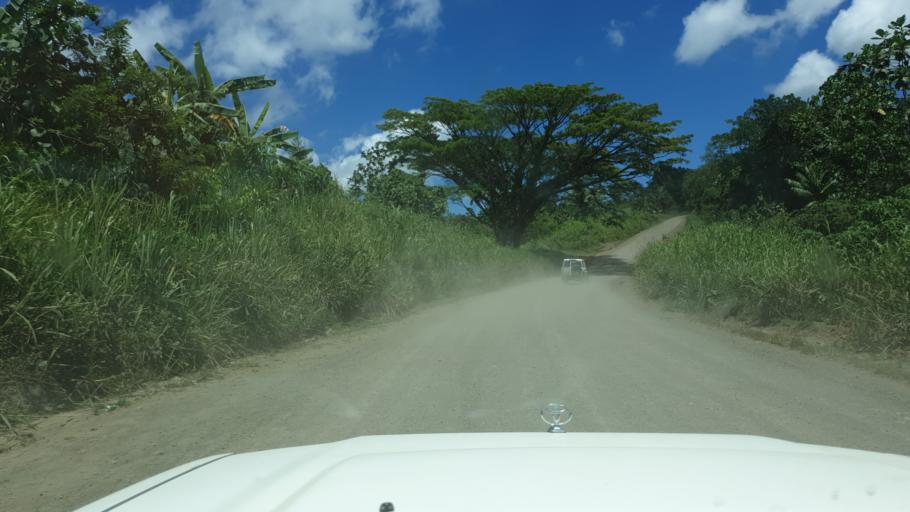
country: PG
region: Madang
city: Madang
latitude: -5.4666
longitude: 145.4892
